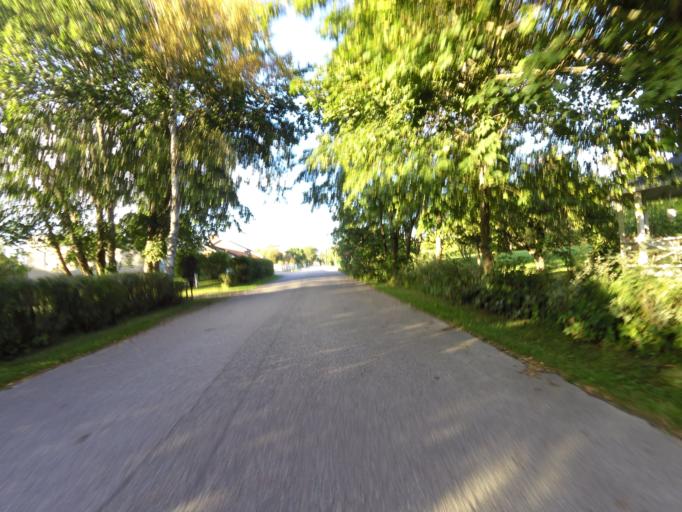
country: SE
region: Gaevleborg
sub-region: Gavle Kommun
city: Gavle
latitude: 60.7213
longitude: 17.1646
